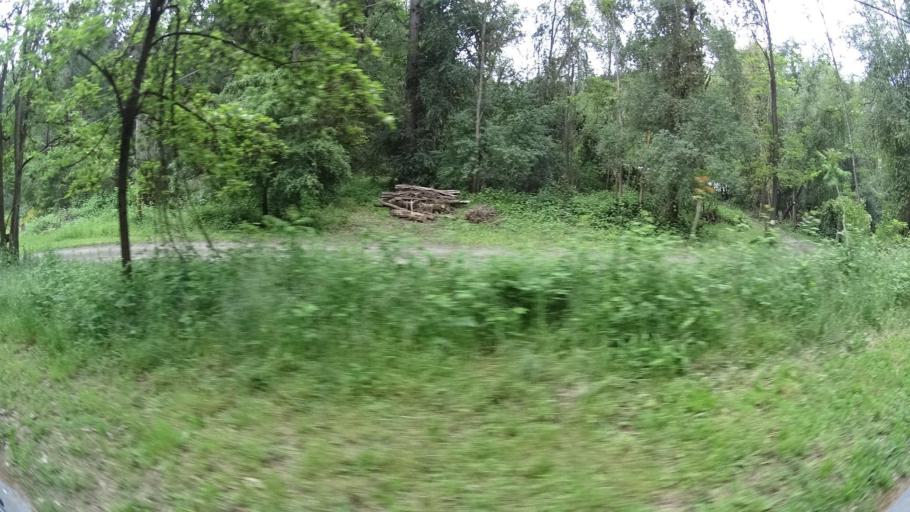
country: US
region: California
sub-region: Humboldt County
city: Willow Creek
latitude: 40.9654
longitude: -123.6343
